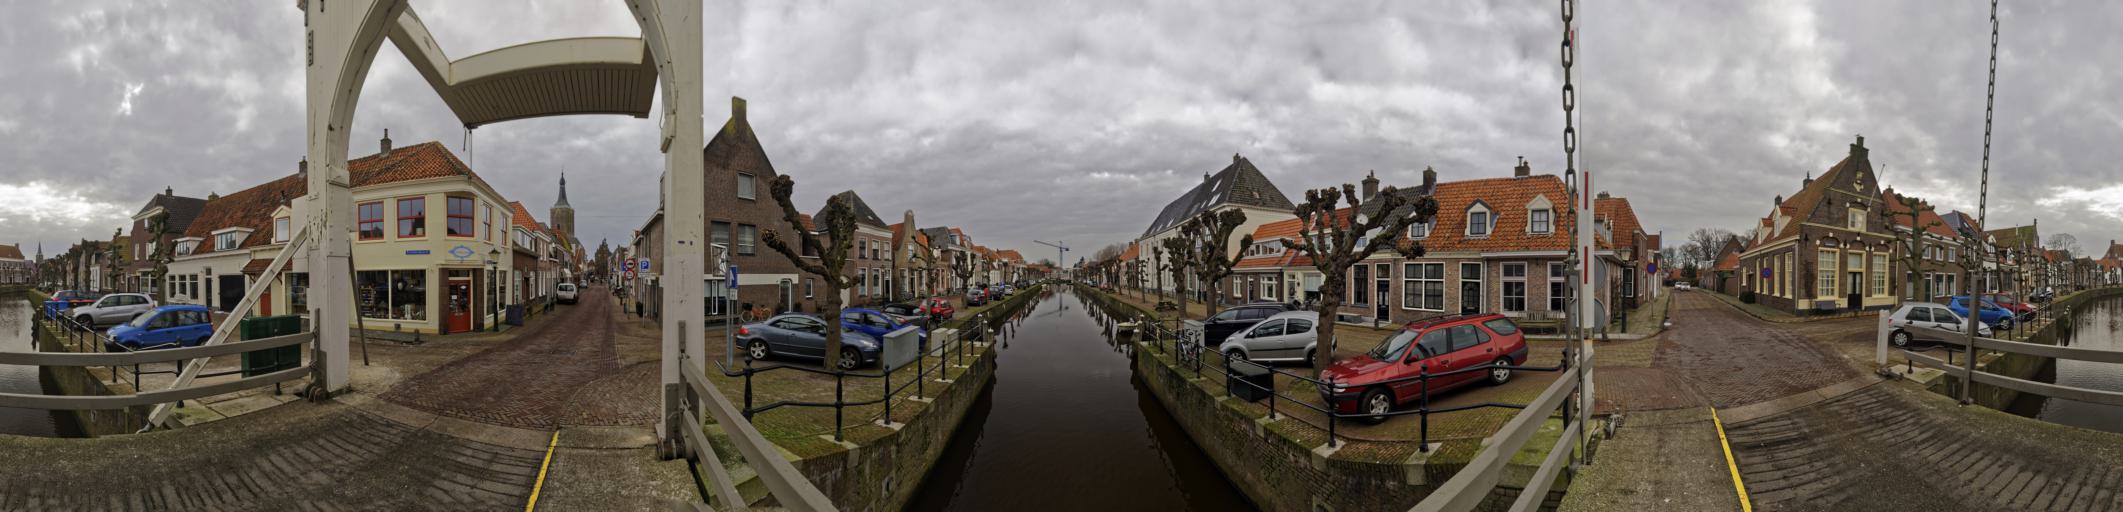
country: NL
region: Overijssel
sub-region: Gemeente Zwartewaterland
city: Hasselt
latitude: 52.5911
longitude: 6.0918
